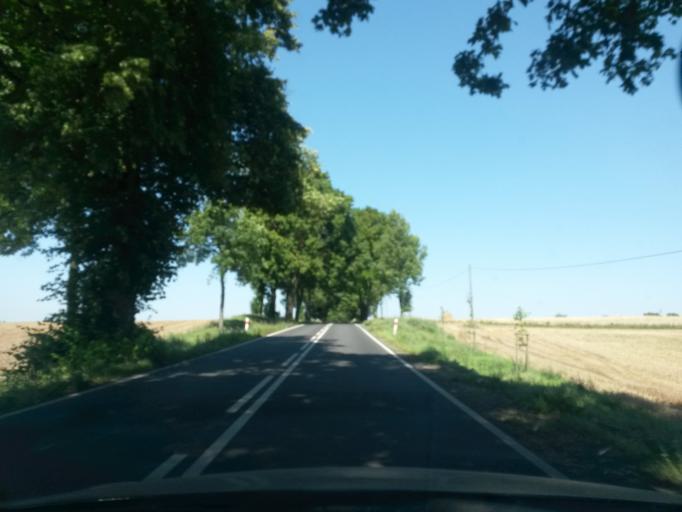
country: PL
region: Warmian-Masurian Voivodeship
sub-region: Powiat ilawski
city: Lubawa
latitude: 53.4034
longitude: 19.8000
